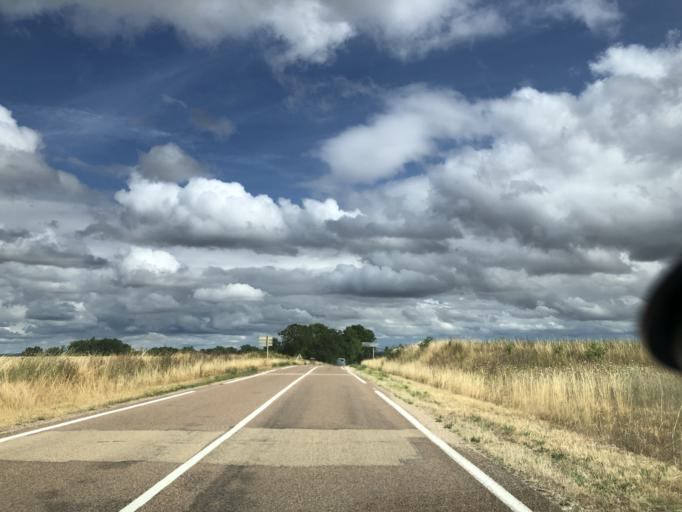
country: FR
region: Bourgogne
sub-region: Departement de l'Yonne
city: Charbuy
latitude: 47.8198
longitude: 3.4532
